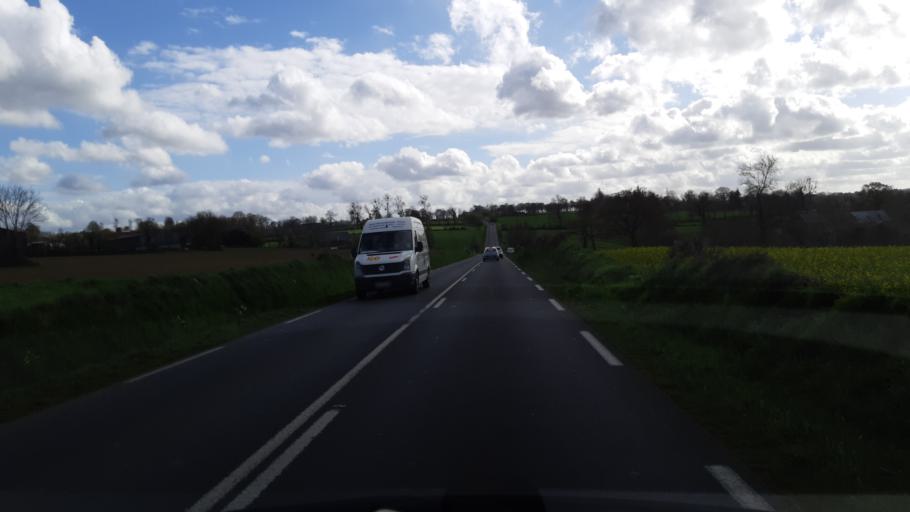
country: FR
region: Lower Normandy
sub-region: Departement de la Manche
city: Agneaux
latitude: 49.0387
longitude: -1.1321
